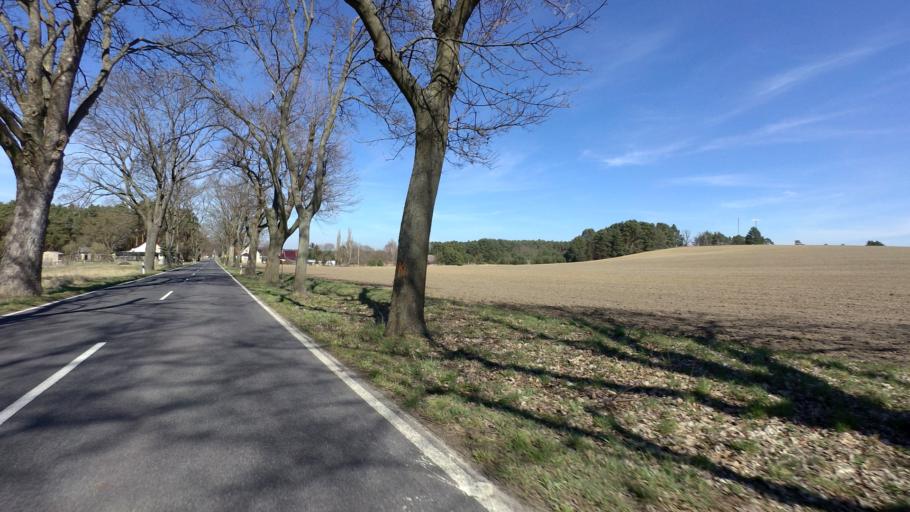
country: DE
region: Brandenburg
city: Storkow
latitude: 52.1890
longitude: 13.9184
